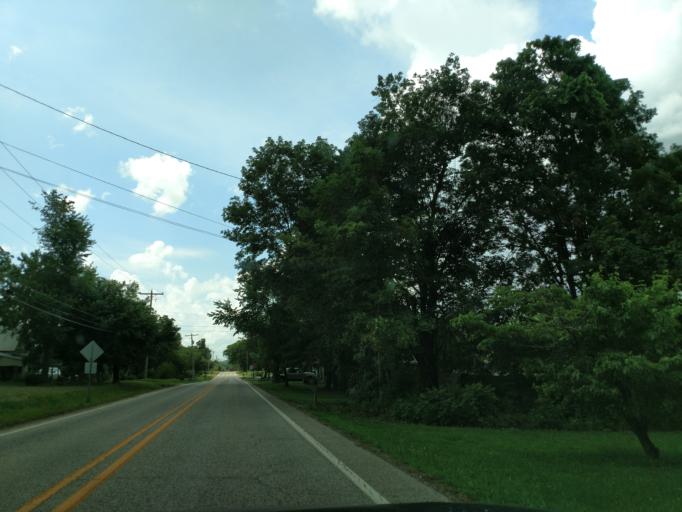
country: US
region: Arkansas
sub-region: Boone County
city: Harrison
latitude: 36.2532
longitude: -93.2213
